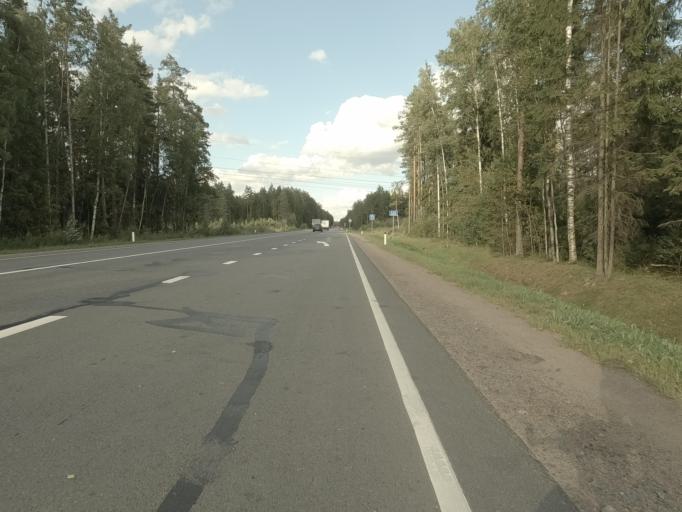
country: RU
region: Leningrad
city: Mga
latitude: 59.7086
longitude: 31.0190
